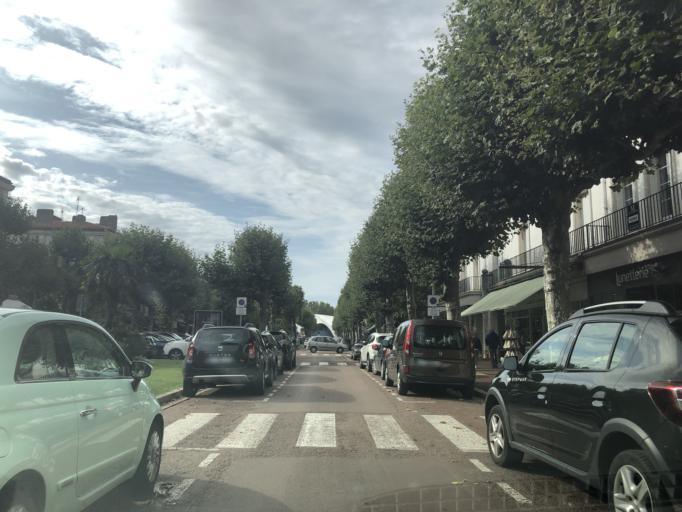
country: FR
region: Poitou-Charentes
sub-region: Departement de la Charente-Maritime
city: Royan
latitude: 45.6257
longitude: -1.0296
